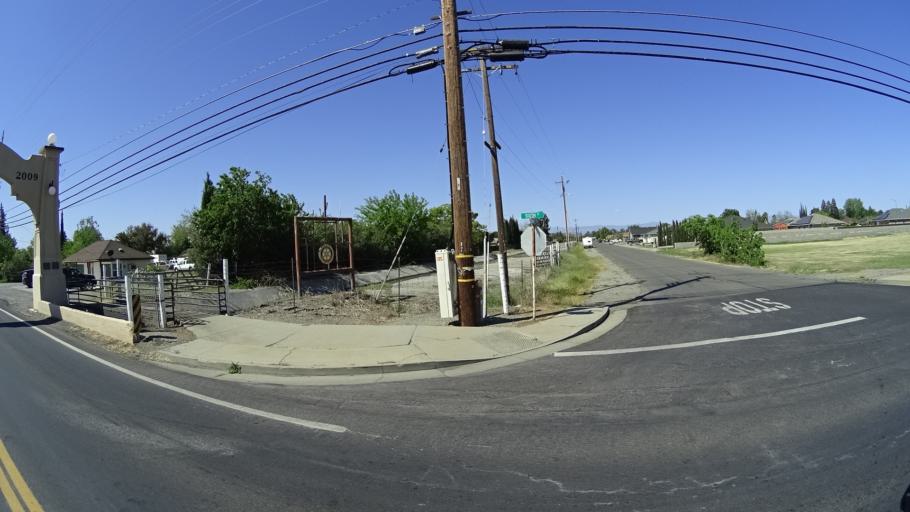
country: US
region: California
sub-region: Glenn County
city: Orland
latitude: 39.7546
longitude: -122.1969
